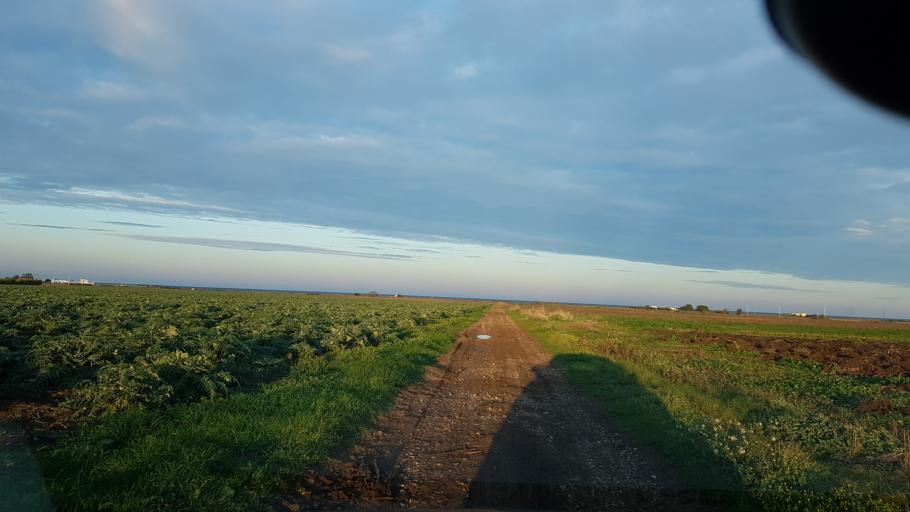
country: IT
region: Apulia
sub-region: Provincia di Brindisi
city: La Rosa
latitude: 40.6070
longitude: 18.0093
